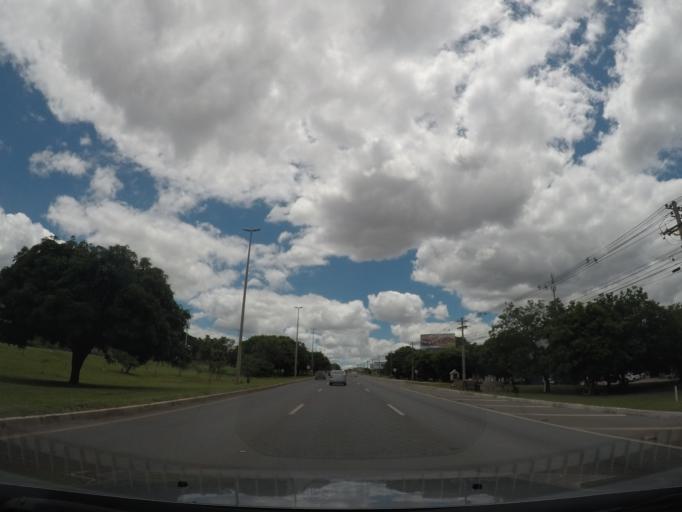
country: BR
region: Federal District
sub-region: Brasilia
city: Brasilia
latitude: -15.7457
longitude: -47.9206
